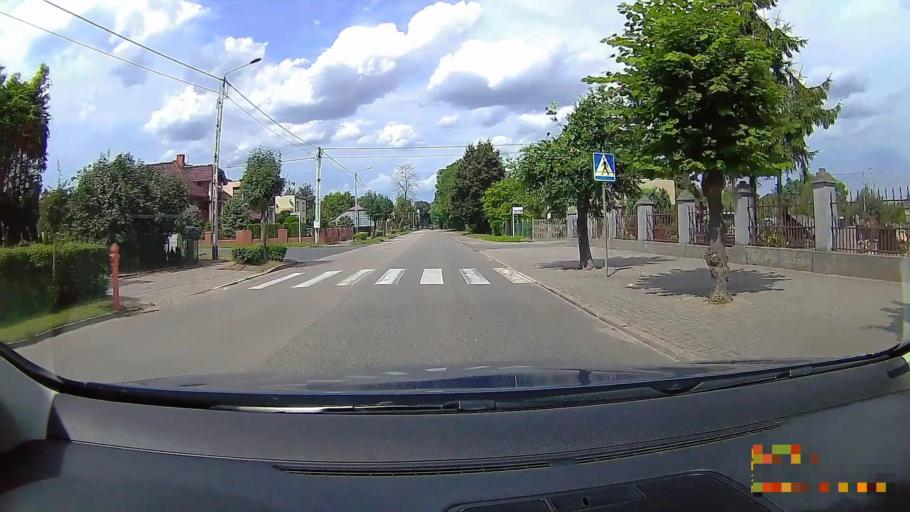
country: PL
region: Greater Poland Voivodeship
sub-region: Powiat koninski
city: Rychwal
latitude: 52.0752
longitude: 18.1624
